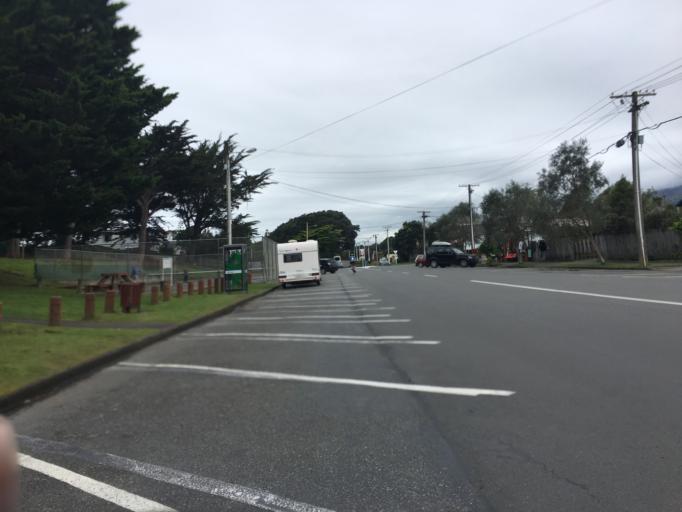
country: NZ
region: Wellington
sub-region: Kapiti Coast District
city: Paraparaumu
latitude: -40.8616
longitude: 175.0238
